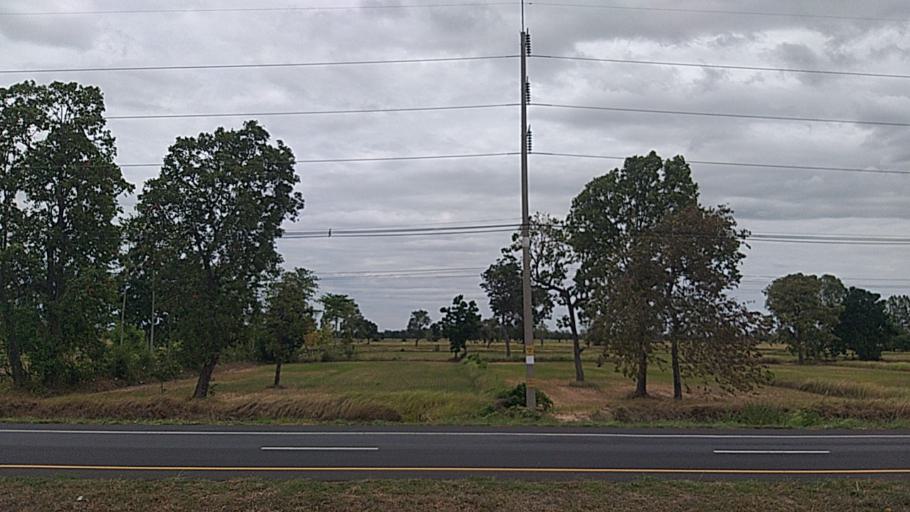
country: TH
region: Buriram
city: Chaloem Phra Kiat
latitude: 14.6070
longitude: 102.9800
